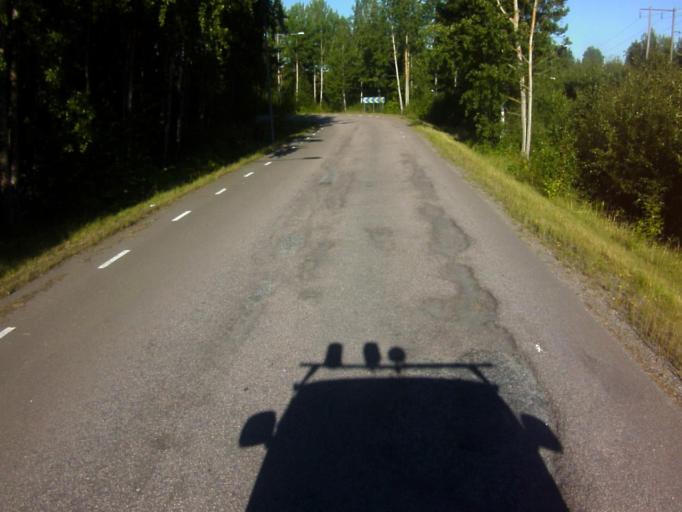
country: SE
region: Soedermanland
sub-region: Eskilstuna Kommun
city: Hallbybrunn
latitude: 59.3970
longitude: 16.4398
